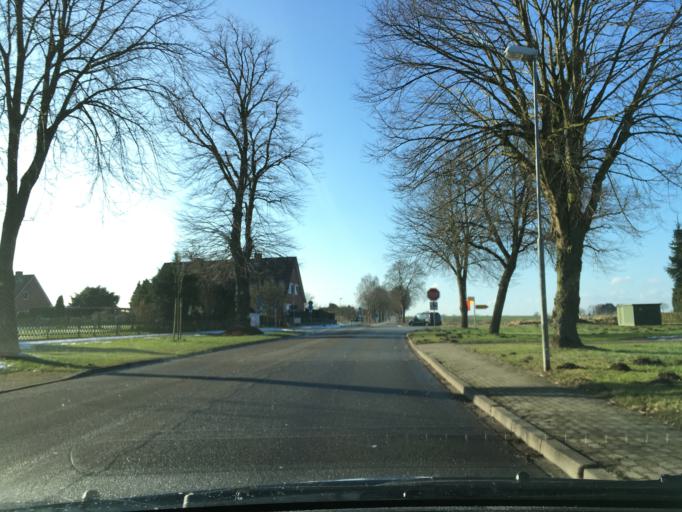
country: DE
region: Schleswig-Holstein
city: Wiershop
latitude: 53.4418
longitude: 10.4485
